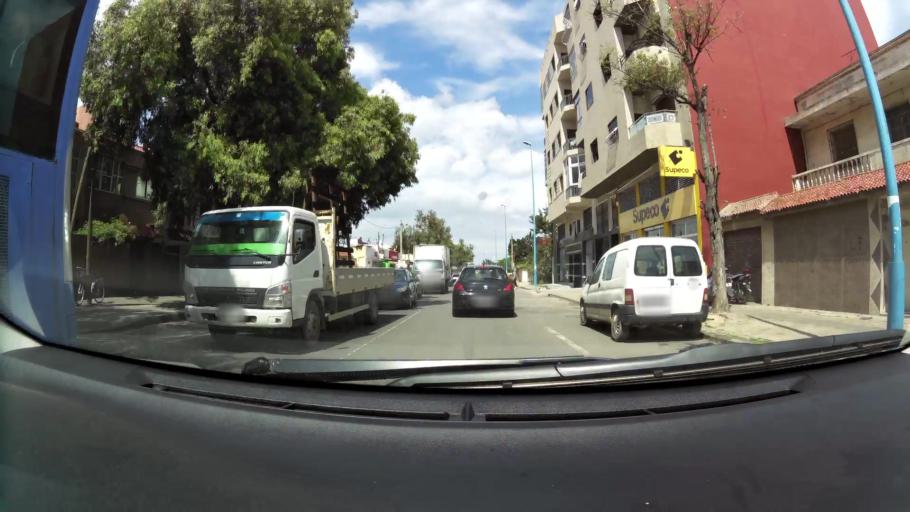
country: MA
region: Grand Casablanca
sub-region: Mediouna
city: Tit Mellil
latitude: 33.6123
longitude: -7.5310
